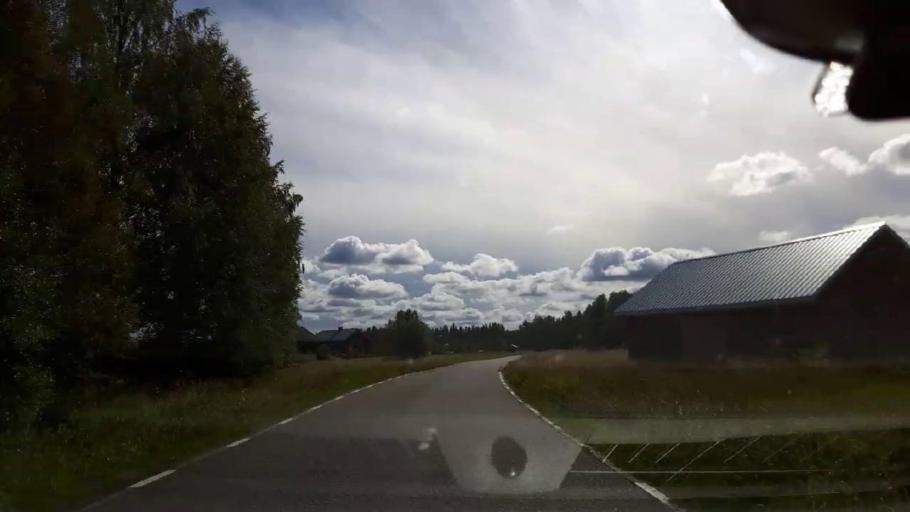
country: SE
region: Jaemtland
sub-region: Braecke Kommun
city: Braecke
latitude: 63.2097
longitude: 15.3503
